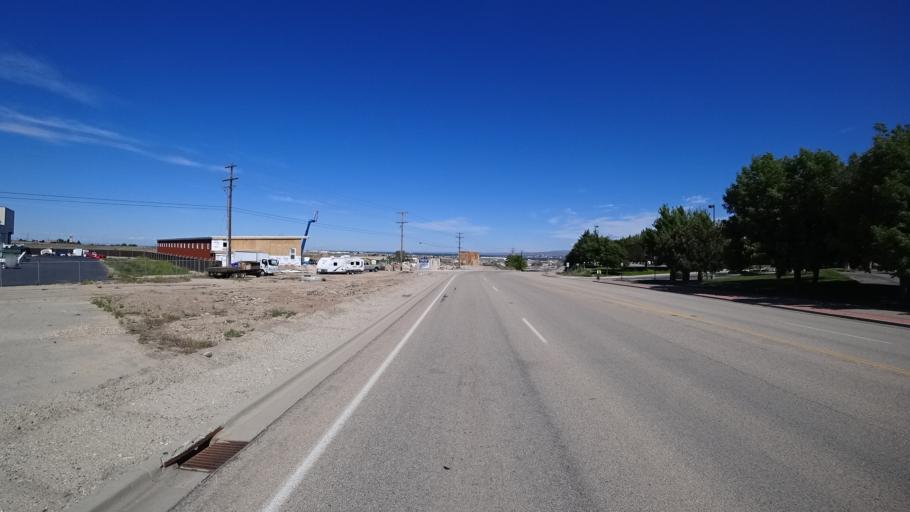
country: US
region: Idaho
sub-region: Ada County
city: Boise
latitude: 43.5440
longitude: -116.1569
